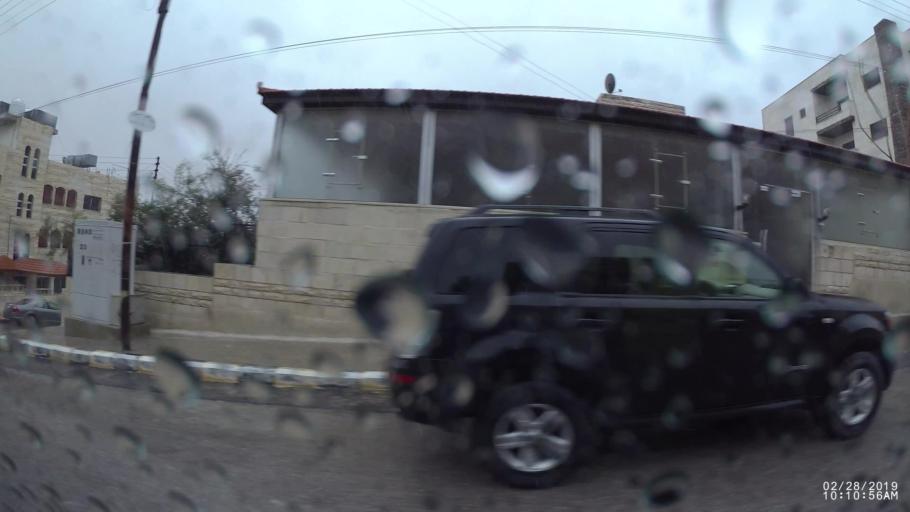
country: JO
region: Amman
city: Al Jubayhah
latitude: 32.0114
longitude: 35.8839
